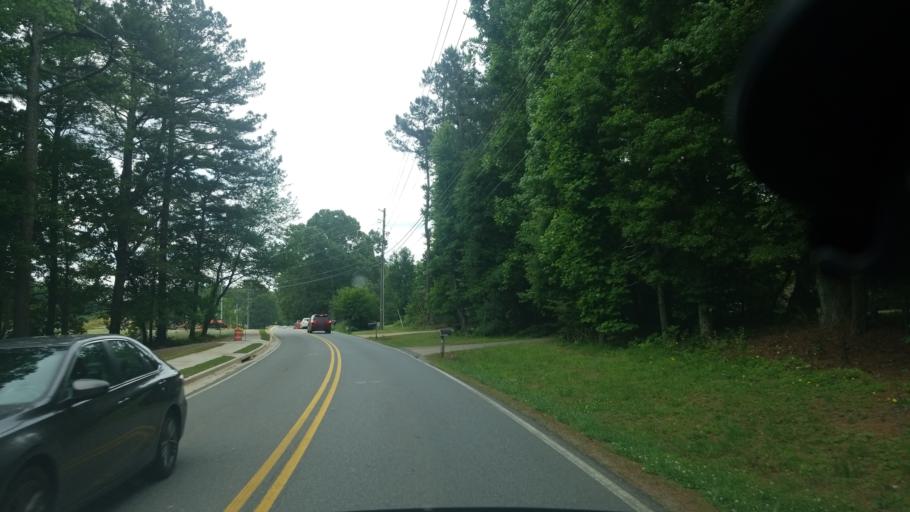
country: US
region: Georgia
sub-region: Forsyth County
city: Cumming
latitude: 34.1361
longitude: -84.1448
